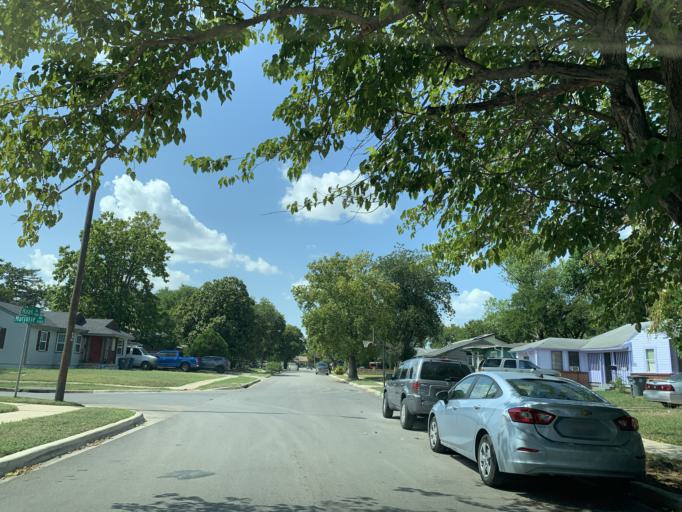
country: US
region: Texas
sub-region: Dallas County
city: Hutchins
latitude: 32.7031
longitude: -96.7674
